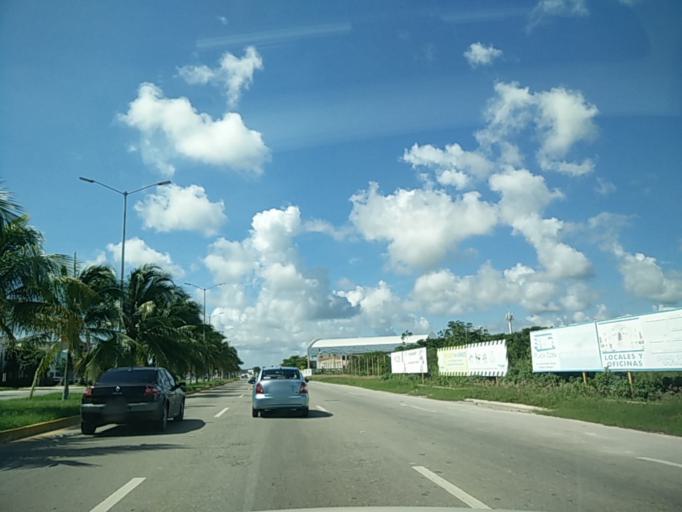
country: MX
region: Quintana Roo
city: Playa del Carmen
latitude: 20.6652
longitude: -87.0714
